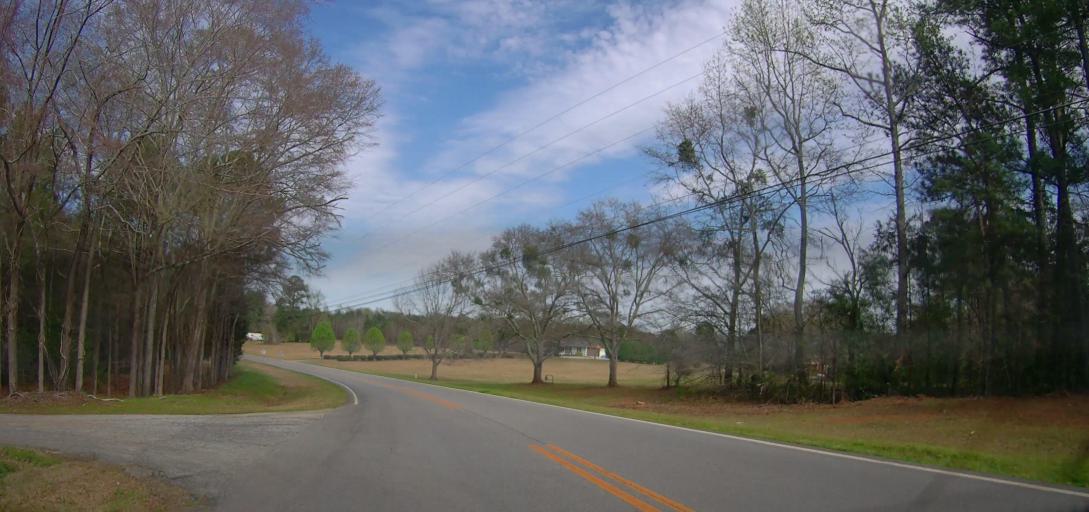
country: US
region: Georgia
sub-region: Monroe County
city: Forsyth
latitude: 33.0452
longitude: -83.9024
